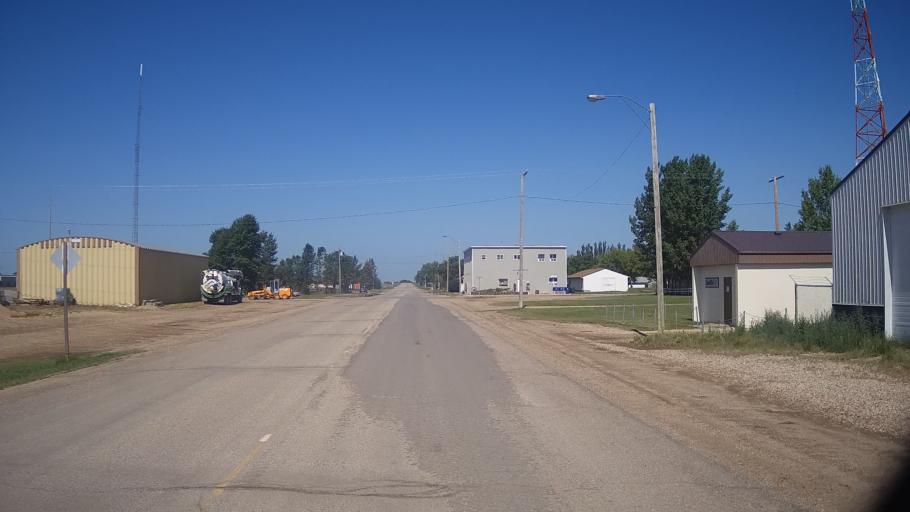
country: CA
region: Saskatchewan
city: Saskatoon
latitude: 51.8926
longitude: -106.0550
